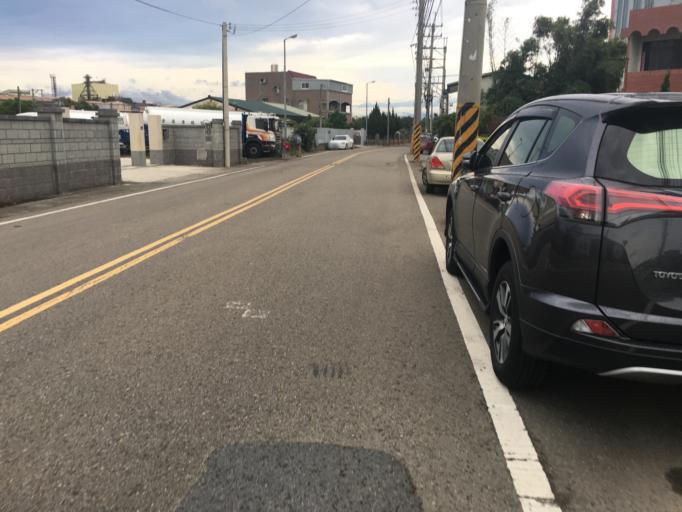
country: TW
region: Taiwan
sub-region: Hsinchu
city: Hsinchu
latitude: 24.7293
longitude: 120.9108
